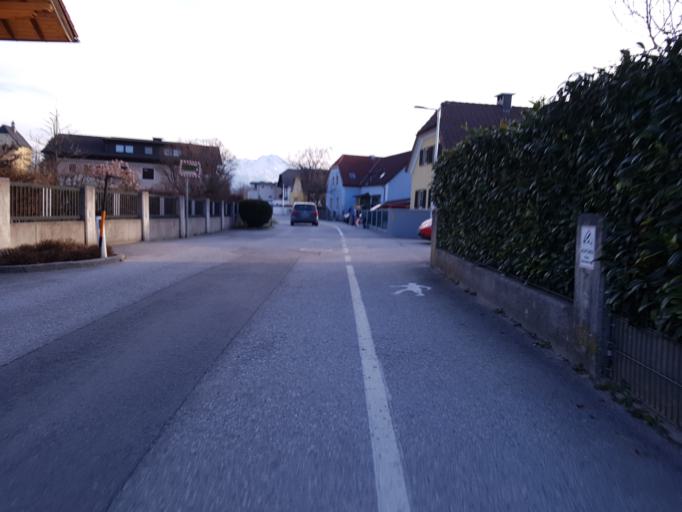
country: AT
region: Salzburg
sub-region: Politischer Bezirk Salzburg-Umgebung
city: Elsbethen
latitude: 47.7623
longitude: 13.0798
